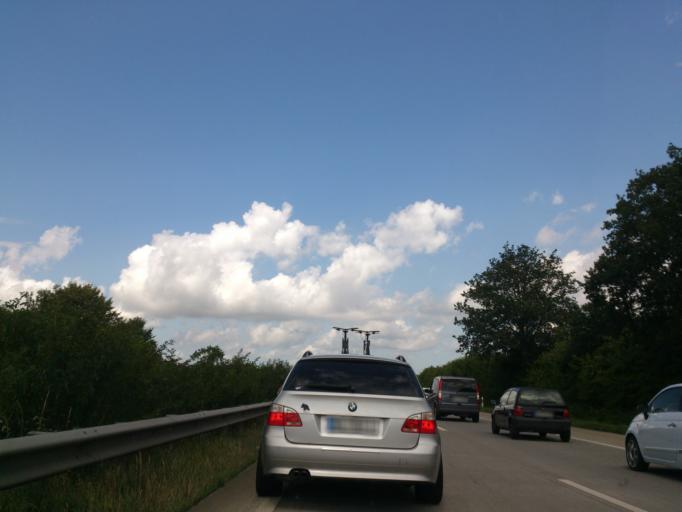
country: DE
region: Schleswig-Holstein
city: Neuenbrook
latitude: 53.8796
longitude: 9.5506
